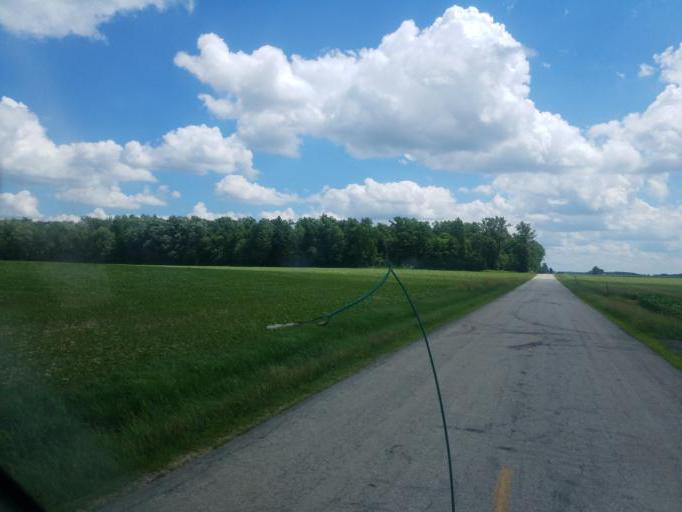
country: US
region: Ohio
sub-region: Crawford County
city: Crestline
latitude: 40.9139
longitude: -82.8264
